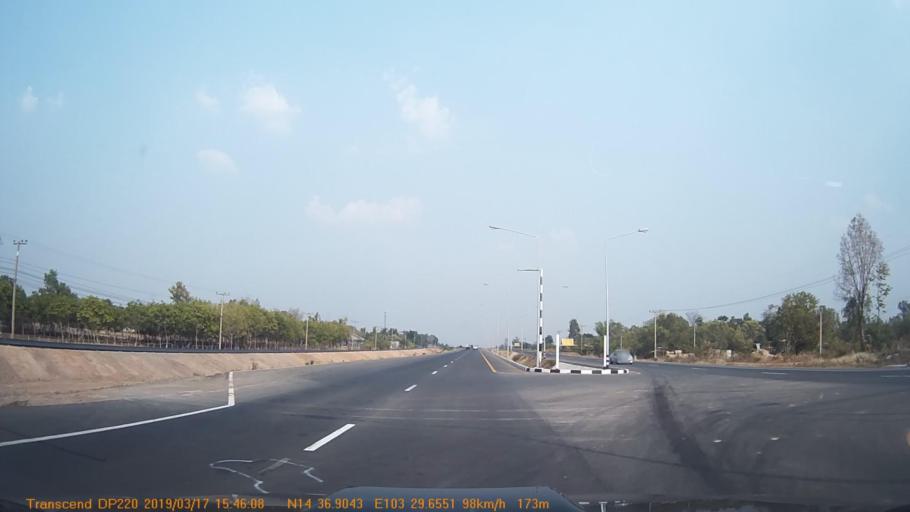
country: TH
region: Surin
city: Prasat
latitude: 14.6150
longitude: 103.4947
